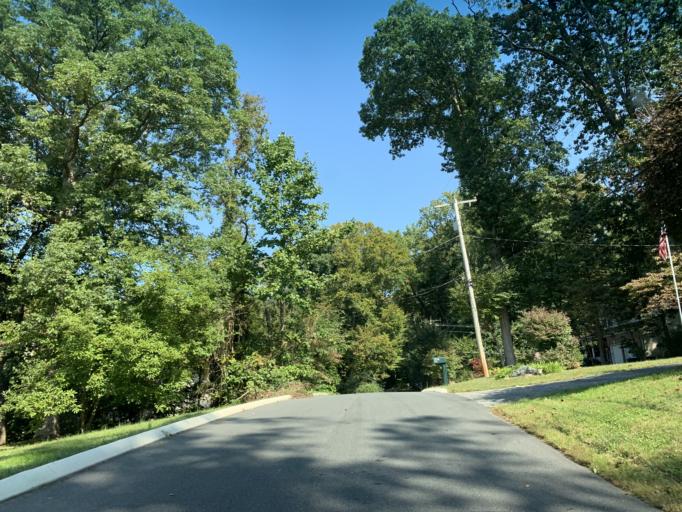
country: US
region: Maryland
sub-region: Harford County
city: South Bel Air
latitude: 39.5251
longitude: -76.3324
